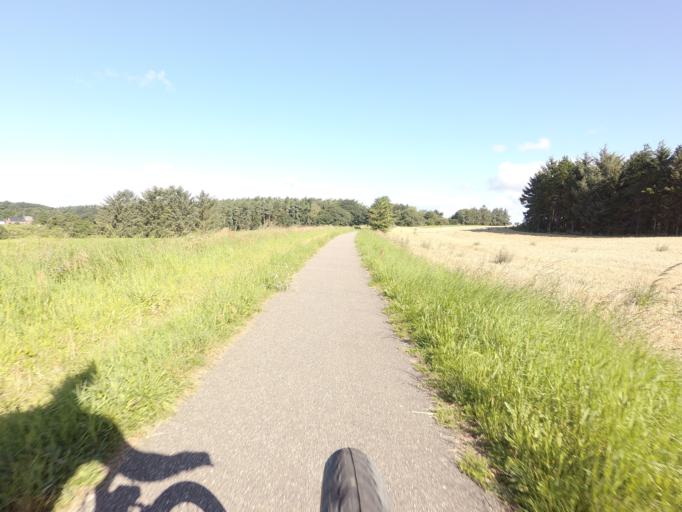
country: DK
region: Central Jutland
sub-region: Horsens Kommune
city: Horsens
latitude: 55.9537
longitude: 9.7744
